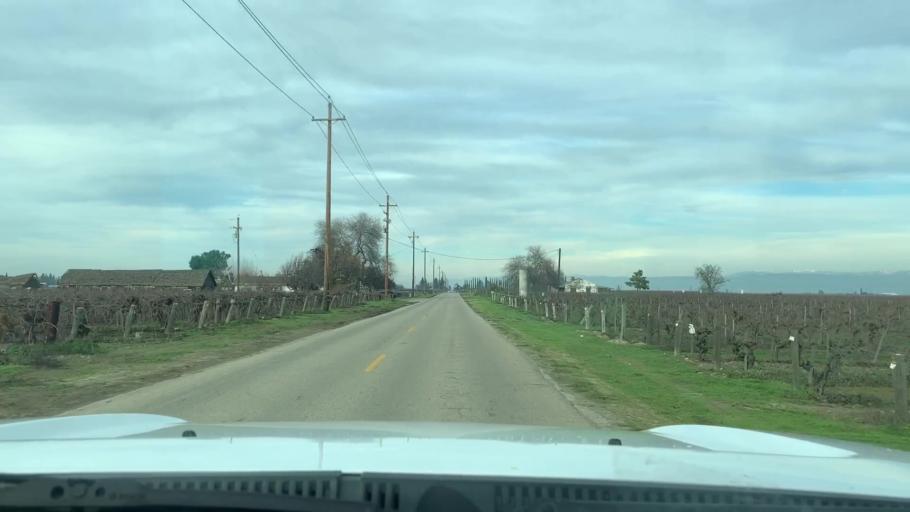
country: US
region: California
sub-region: Fresno County
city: Selma
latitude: 36.5934
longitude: -119.5748
